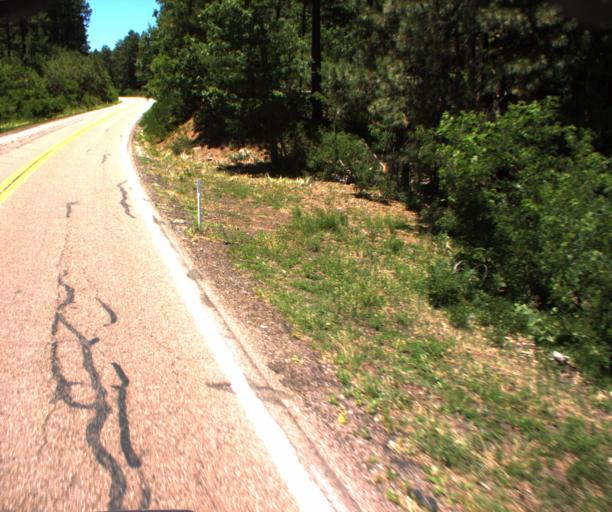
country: US
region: Arizona
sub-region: Gila County
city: Pine
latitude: 34.4630
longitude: -111.3868
